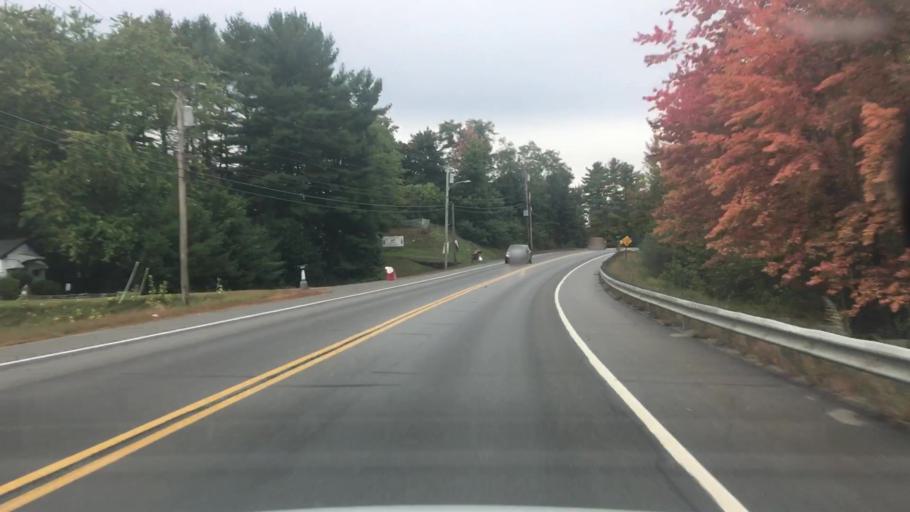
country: US
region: Maine
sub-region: Kennebec County
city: Augusta
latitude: 44.3795
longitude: -69.8012
